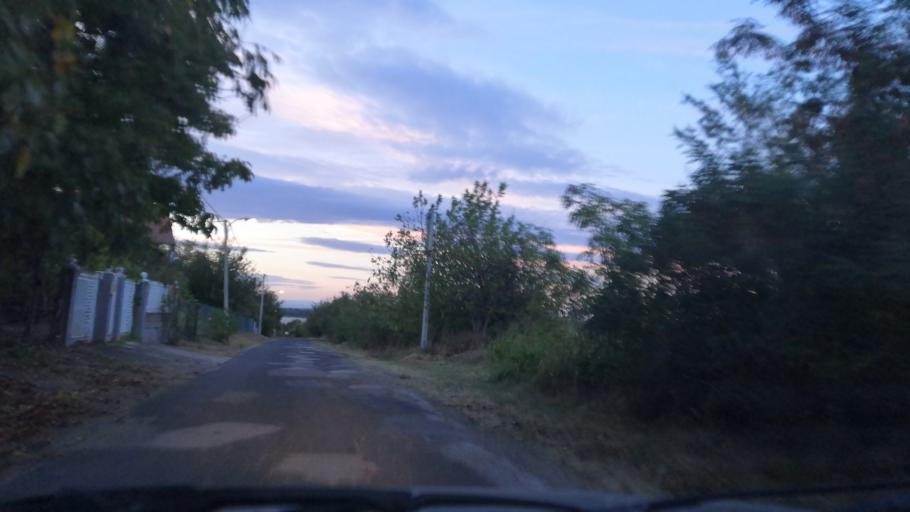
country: RO
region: Mehedinti
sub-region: Comuna Gogosu
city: Balta Verde
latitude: 44.3122
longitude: 22.5483
